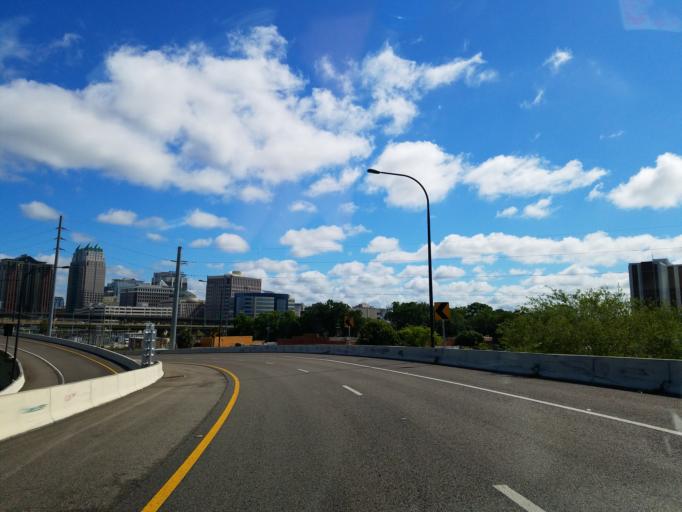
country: US
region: Florida
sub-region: Orange County
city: Orlando
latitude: 28.5322
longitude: -81.3835
